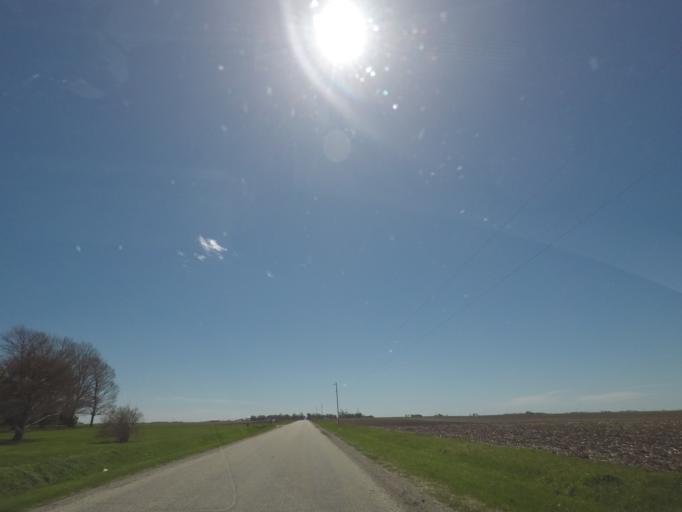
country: US
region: Illinois
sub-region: Logan County
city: Atlanta
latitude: 40.1601
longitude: -89.1935
